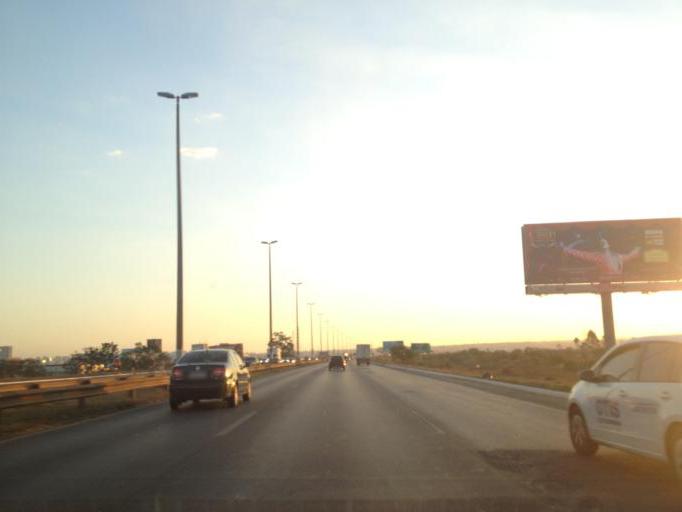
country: BR
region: Federal District
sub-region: Brasilia
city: Brasilia
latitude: -15.7947
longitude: -47.9613
